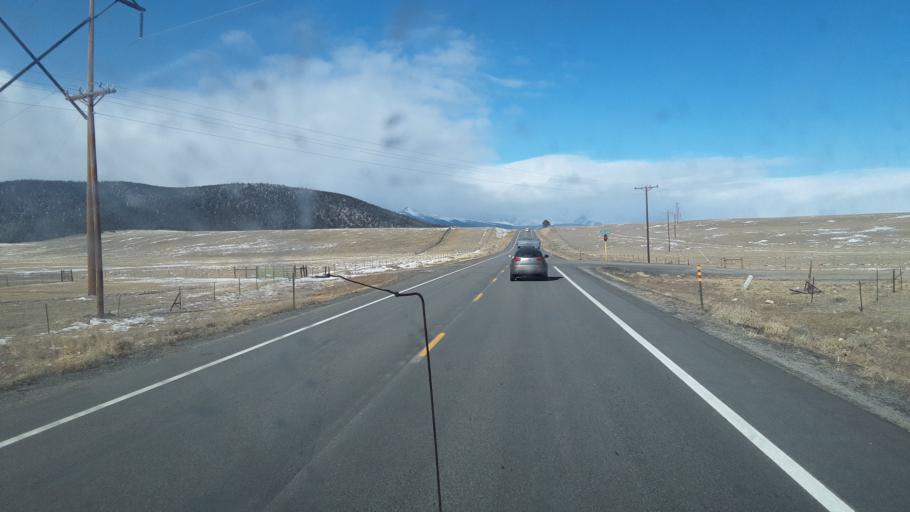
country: US
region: Colorado
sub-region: Park County
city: Fairplay
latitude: 39.0846
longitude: -105.9784
